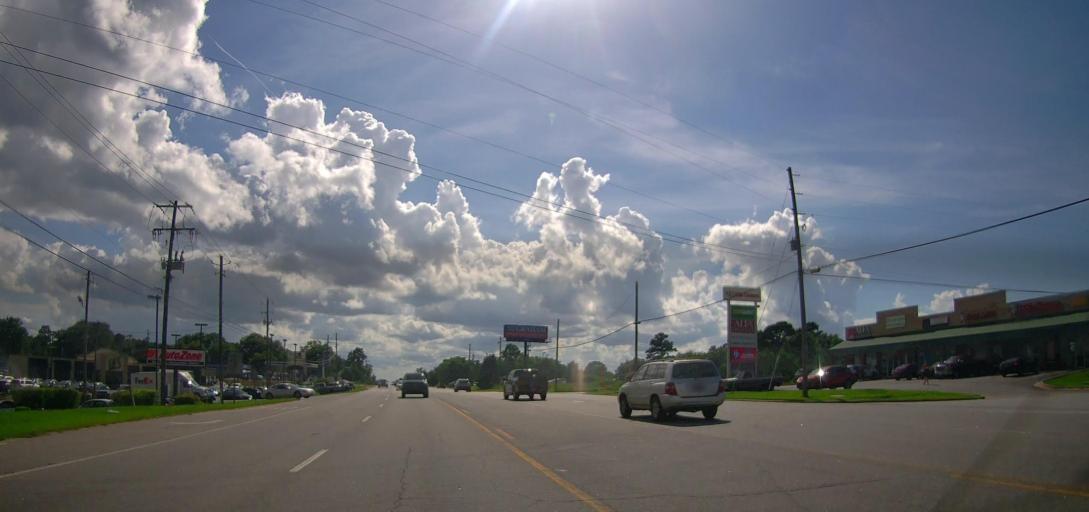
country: US
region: Alabama
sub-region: Russell County
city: Ladonia
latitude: 32.4701
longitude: -85.0988
